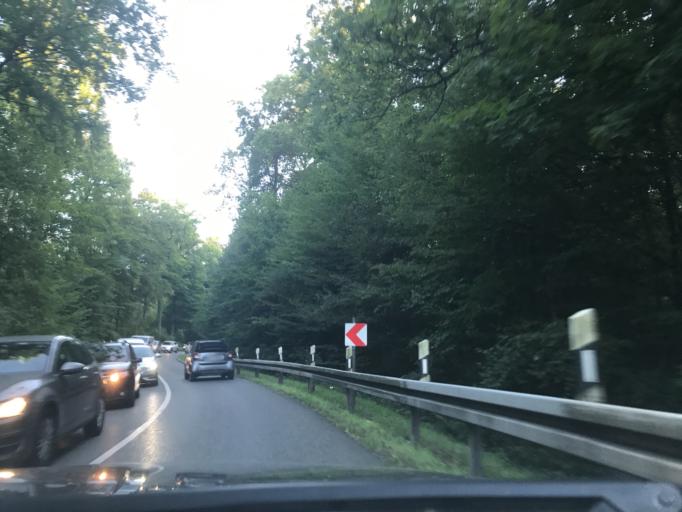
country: DE
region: Baden-Wuerttemberg
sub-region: Regierungsbezirk Stuttgart
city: Gerlingen
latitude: 48.7920
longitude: 9.0917
